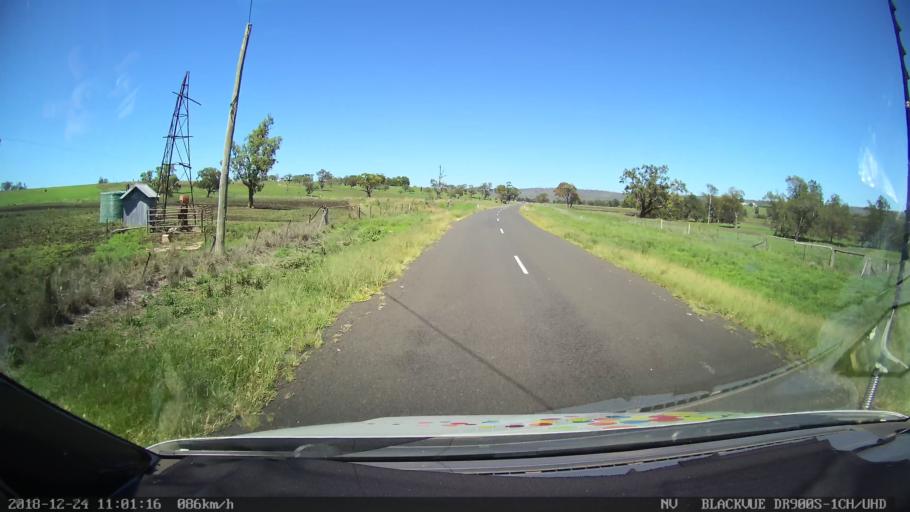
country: AU
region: New South Wales
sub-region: Upper Hunter Shire
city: Merriwa
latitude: -32.0756
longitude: 150.3858
